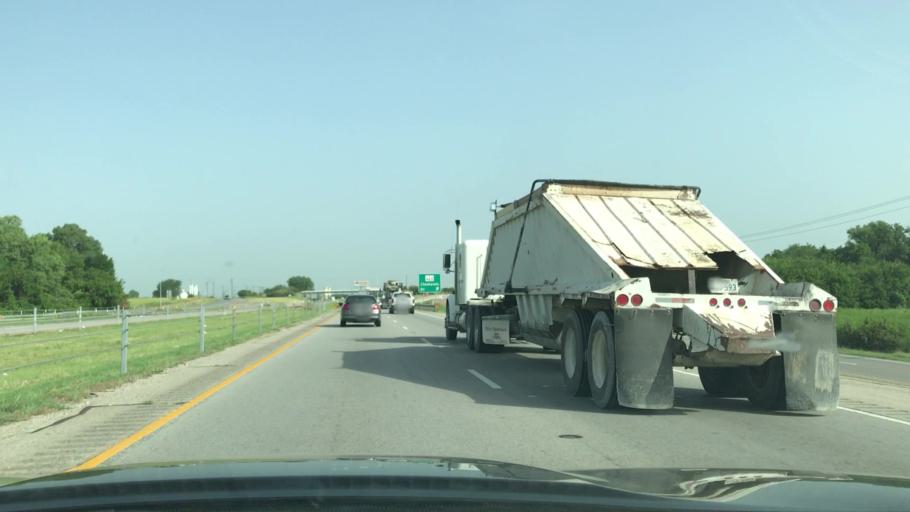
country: US
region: Texas
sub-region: Kaufman County
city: Forney
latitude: 32.7660
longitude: -96.4846
